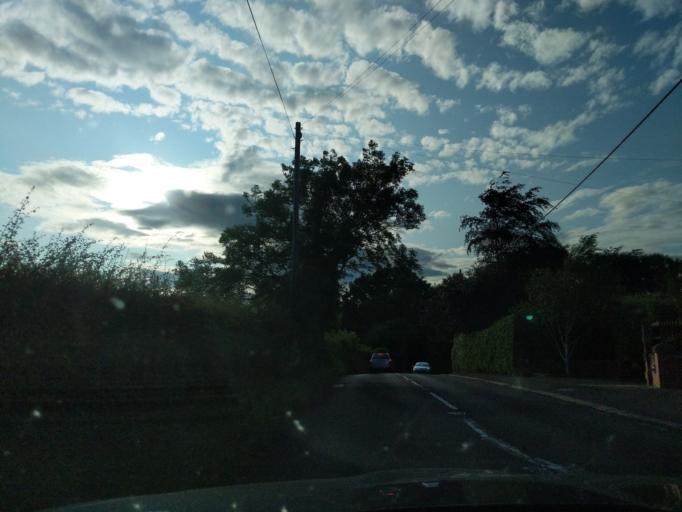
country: GB
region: England
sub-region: Northumberland
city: Bedlington
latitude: 55.1236
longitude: -1.5804
